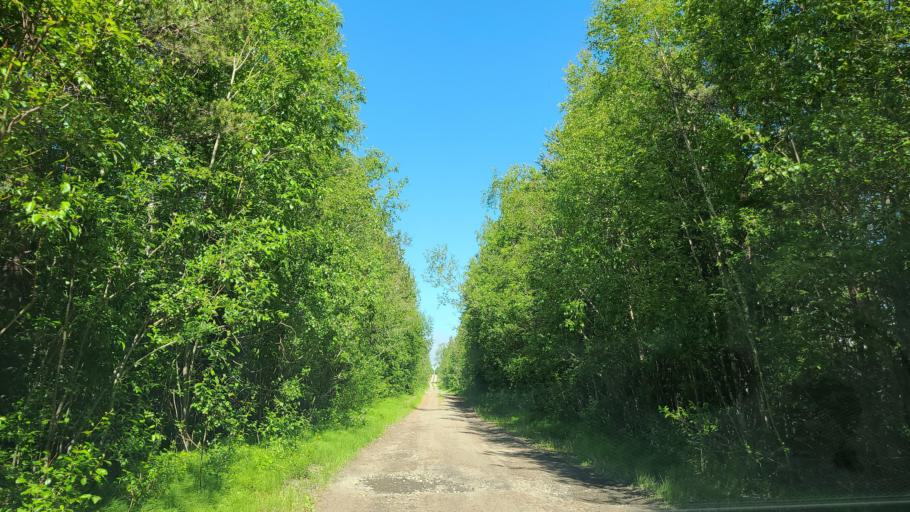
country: SE
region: Vaesternorrland
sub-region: OErnskoeldsviks Kommun
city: Husum
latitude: 63.4284
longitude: 19.2273
